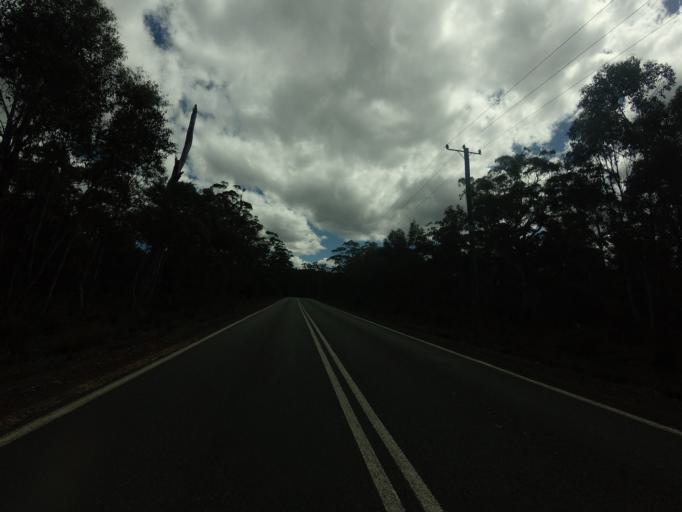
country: AU
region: Tasmania
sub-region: Northern Midlands
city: Evandale
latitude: -42.0245
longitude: 147.7687
